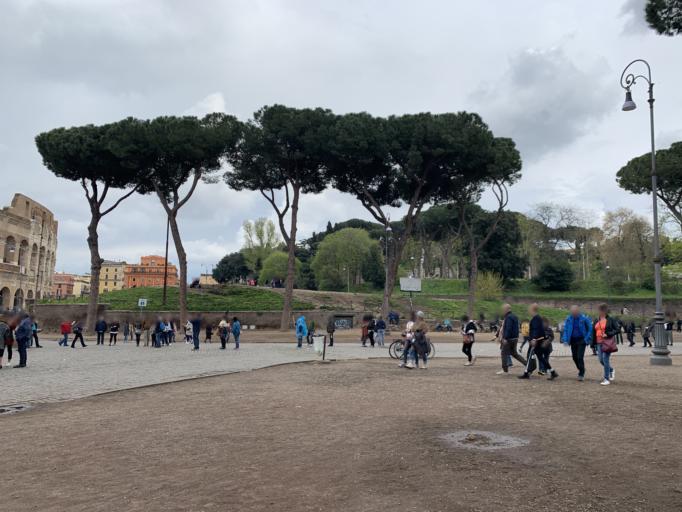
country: IT
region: Latium
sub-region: Citta metropolitana di Roma Capitale
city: Rome
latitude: 41.8896
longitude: 12.4903
